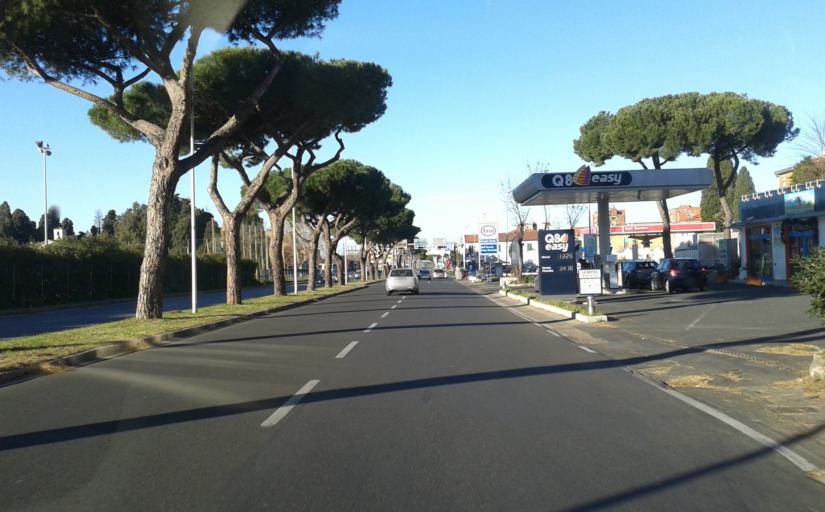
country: IT
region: Tuscany
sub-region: Provincia di Livorno
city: Livorno
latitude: 43.5609
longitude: 10.3262
